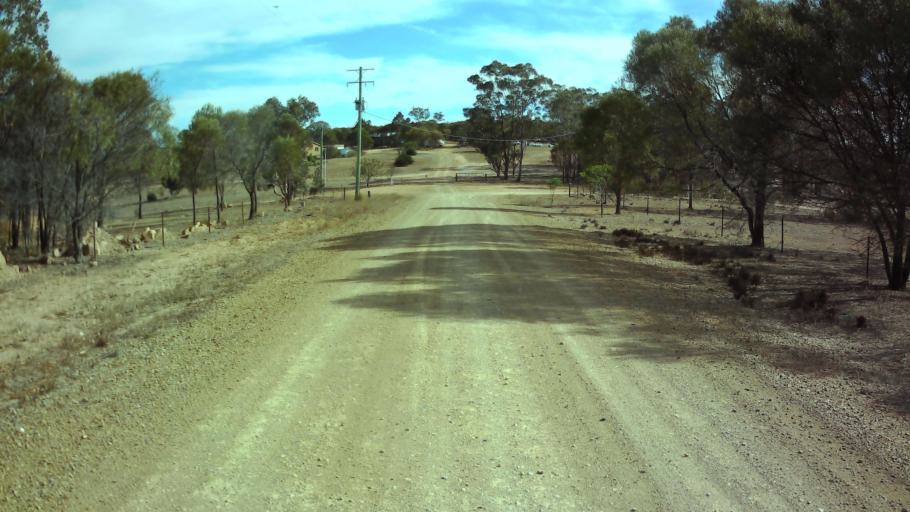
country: AU
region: New South Wales
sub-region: Weddin
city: Grenfell
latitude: -33.8707
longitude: 148.1923
